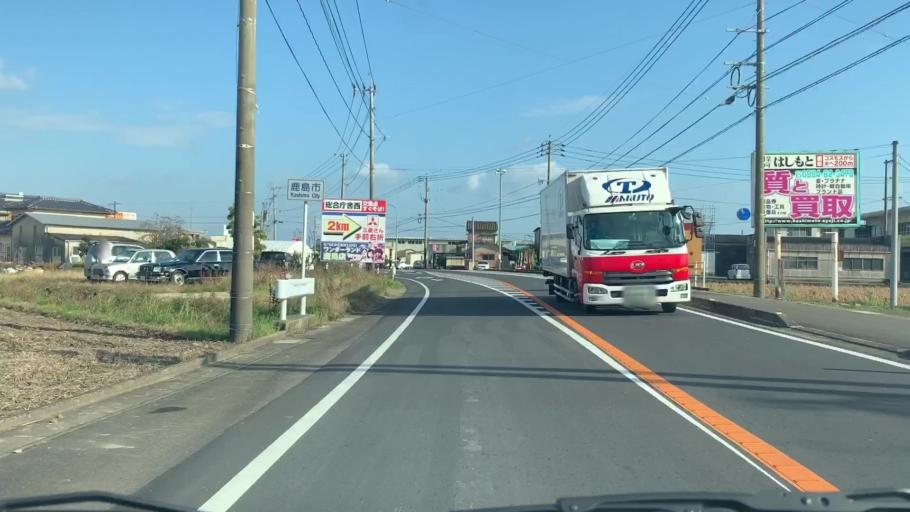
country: JP
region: Saga Prefecture
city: Kashima
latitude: 33.1222
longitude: 130.0835
